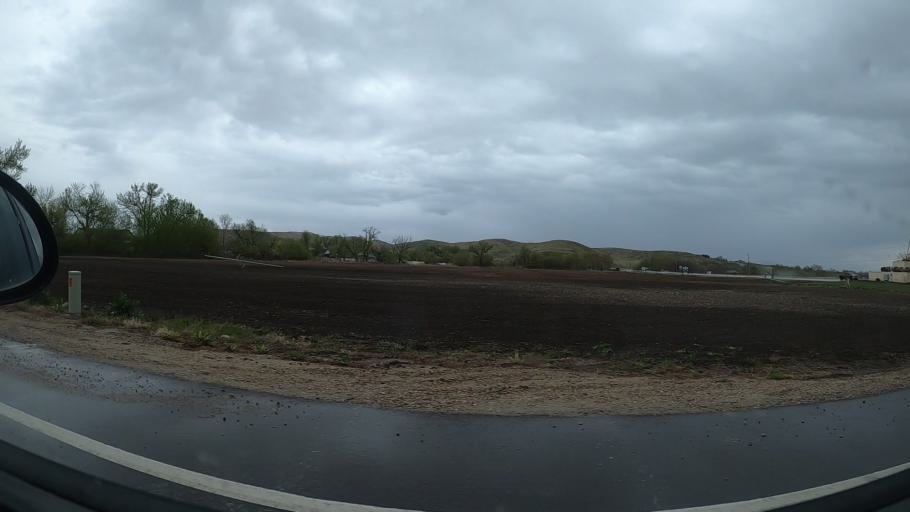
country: US
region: Idaho
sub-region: Ada County
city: Eagle
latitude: 43.7356
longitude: -116.3033
